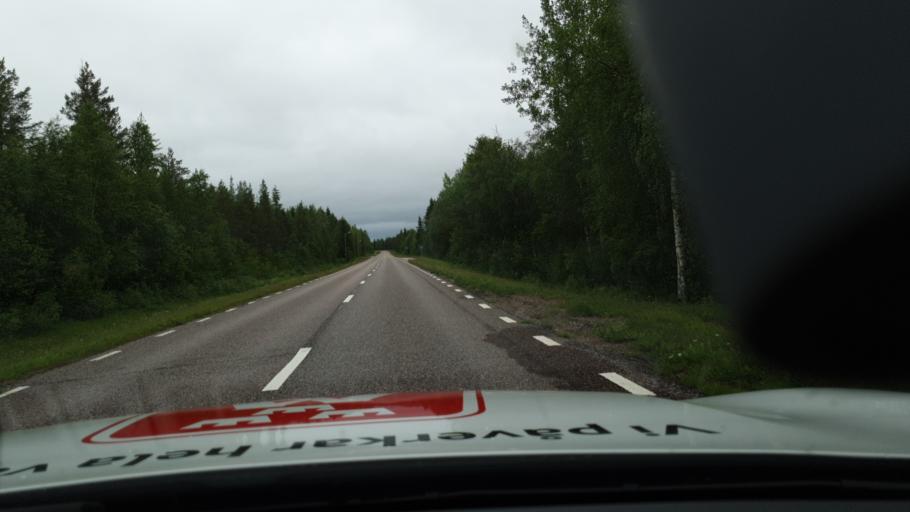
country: FI
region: Lapland
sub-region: Tunturi-Lappi
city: Kolari
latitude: 67.0773
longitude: 23.6605
